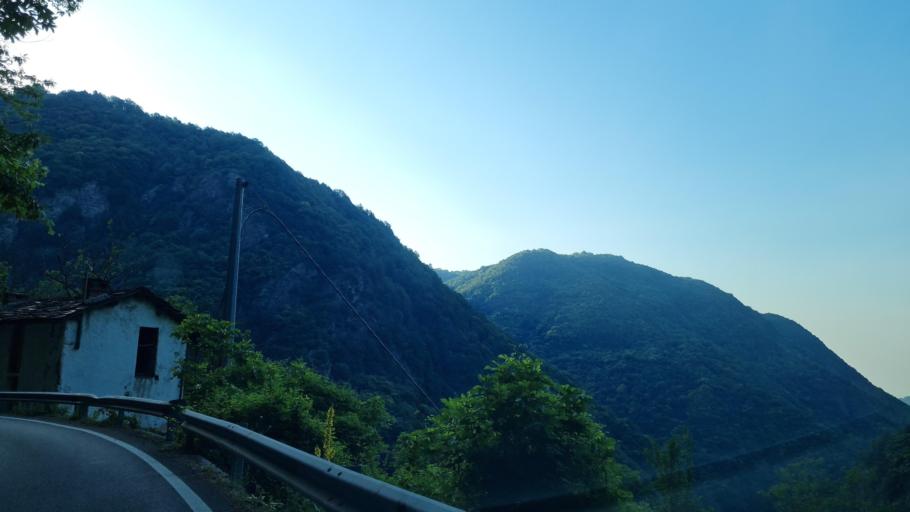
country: IT
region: Piedmont
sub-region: Provincia di Torino
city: Ingria
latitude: 45.4479
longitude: 7.5819
